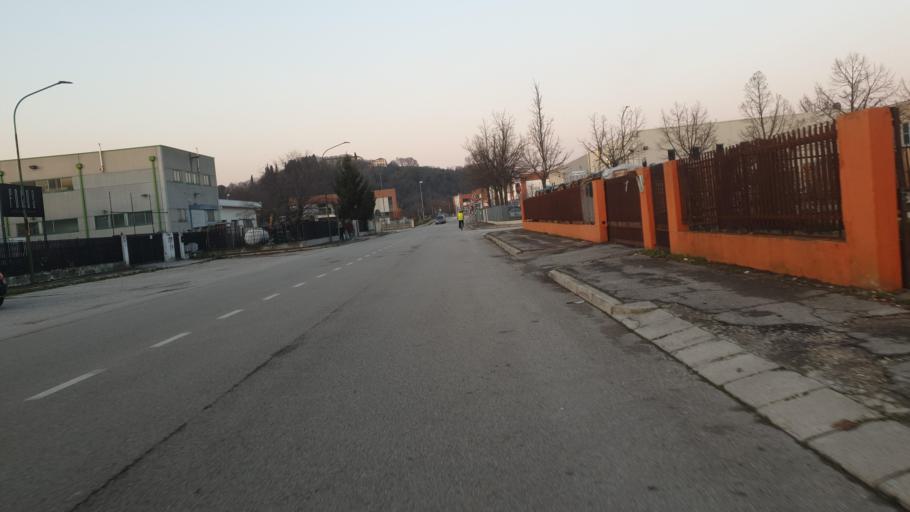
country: IT
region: Veneto
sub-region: Provincia di Padova
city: Montegrotto Terme
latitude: 45.3374
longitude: 11.7657
